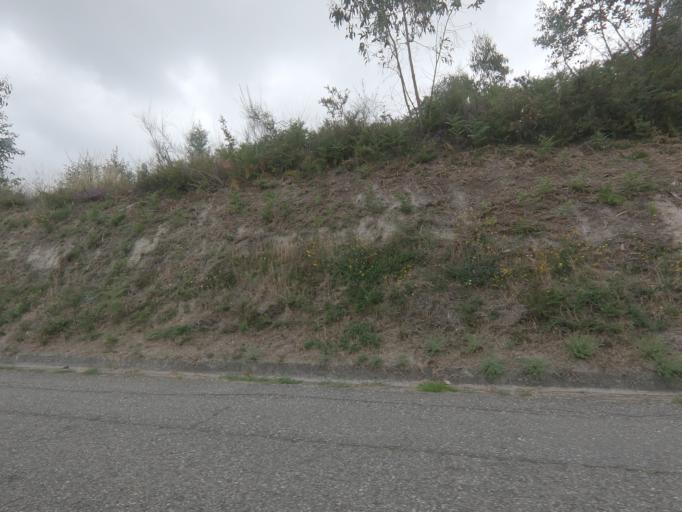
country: ES
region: Galicia
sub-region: Provincia de Pontevedra
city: Tui
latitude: 42.0480
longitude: -8.6573
